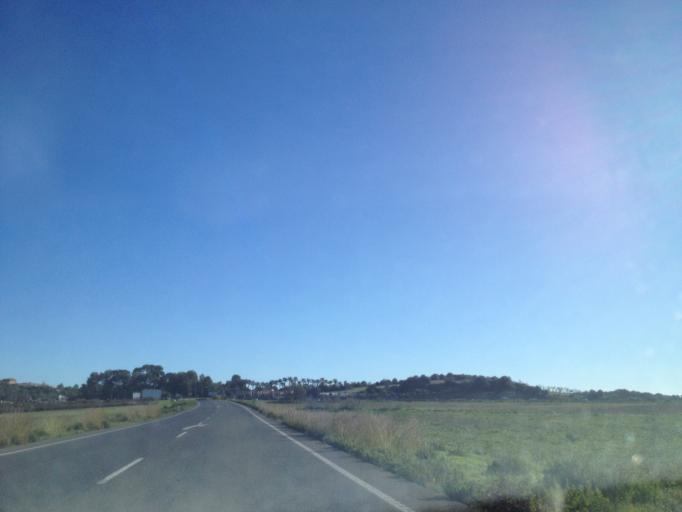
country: ES
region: Balearic Islands
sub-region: Illes Balears
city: Ariany
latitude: 39.6459
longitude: 3.0950
